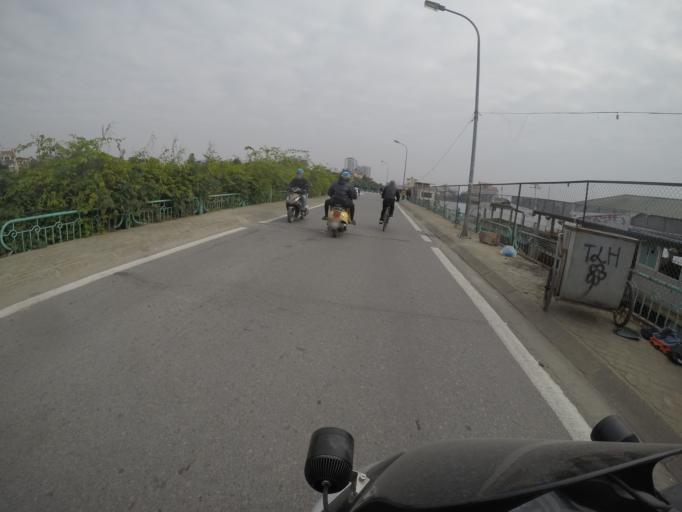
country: VN
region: Ha Noi
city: Tay Ho
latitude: 21.0735
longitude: 105.8202
